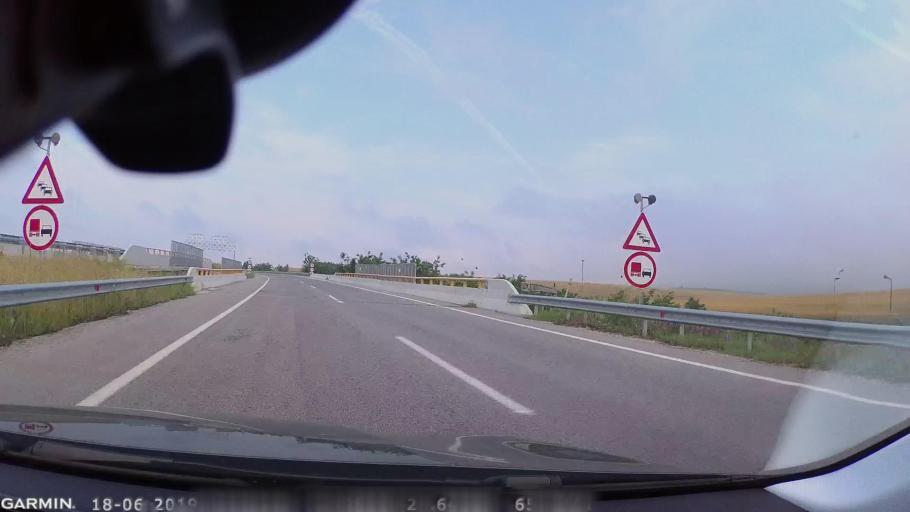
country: MK
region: Petrovec
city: Sredno Konjare
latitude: 41.9536
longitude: 21.7528
